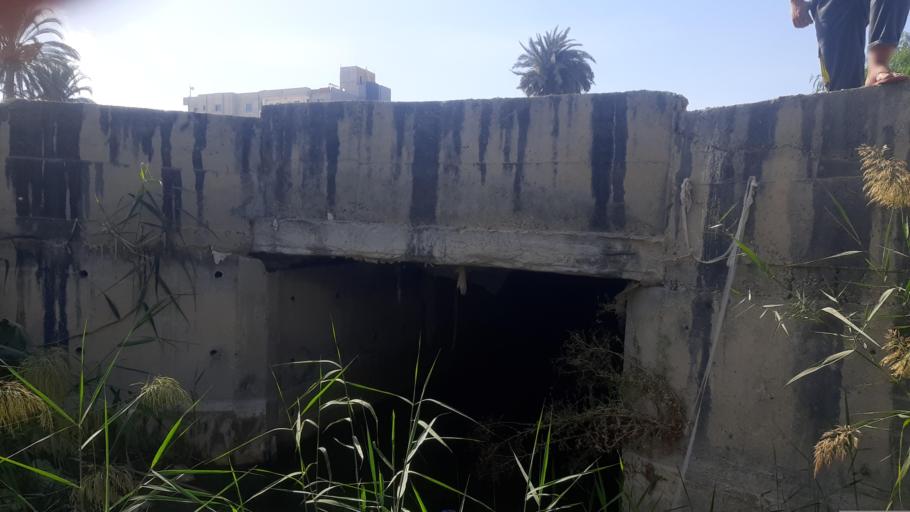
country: TN
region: Qabis
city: Gabes
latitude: 33.8722
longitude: 10.0962
